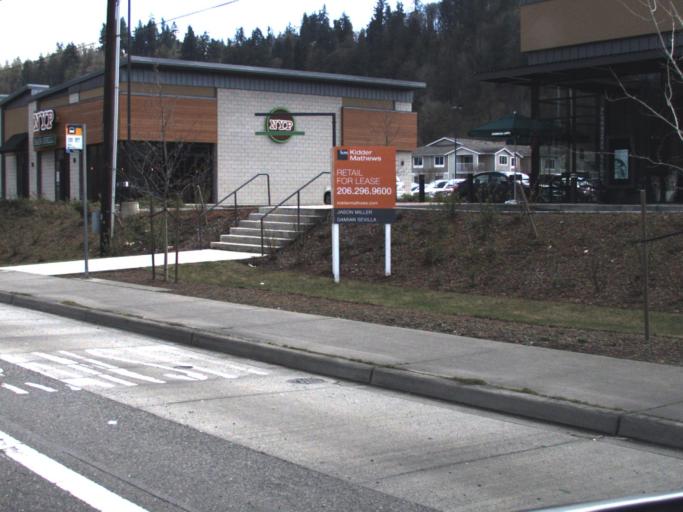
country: US
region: Washington
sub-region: King County
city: Fairwood
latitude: 47.4652
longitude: -122.1370
